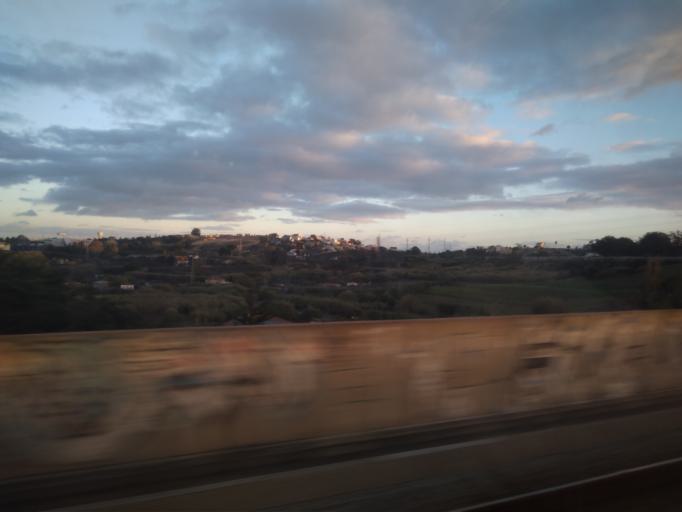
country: PT
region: Setubal
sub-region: Almada
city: Sobreda
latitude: 38.6623
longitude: -9.1858
